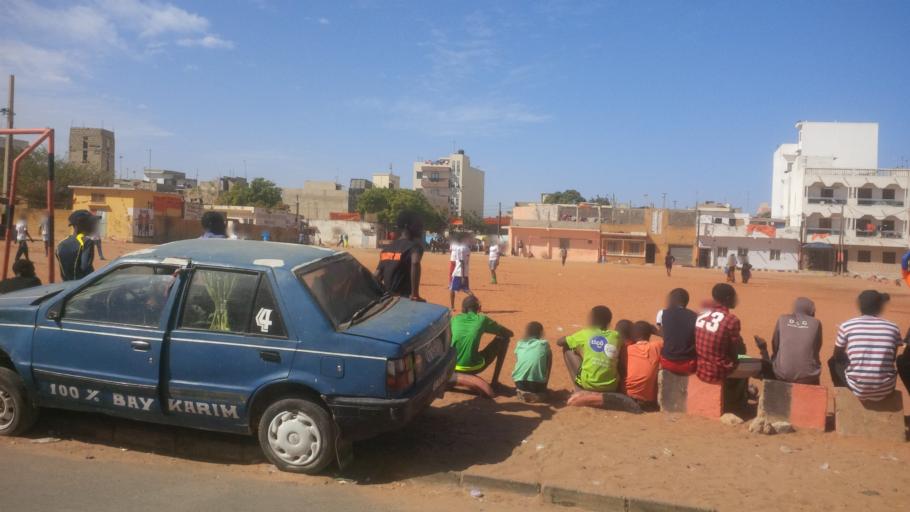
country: SN
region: Dakar
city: Pikine
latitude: 14.7781
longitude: -17.3721
